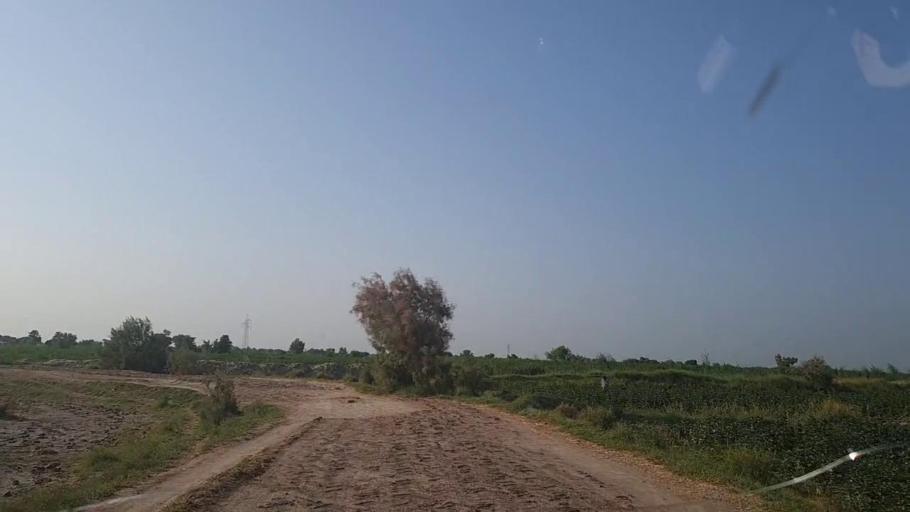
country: PK
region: Sindh
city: Khanpur
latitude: 27.7288
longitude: 69.3069
